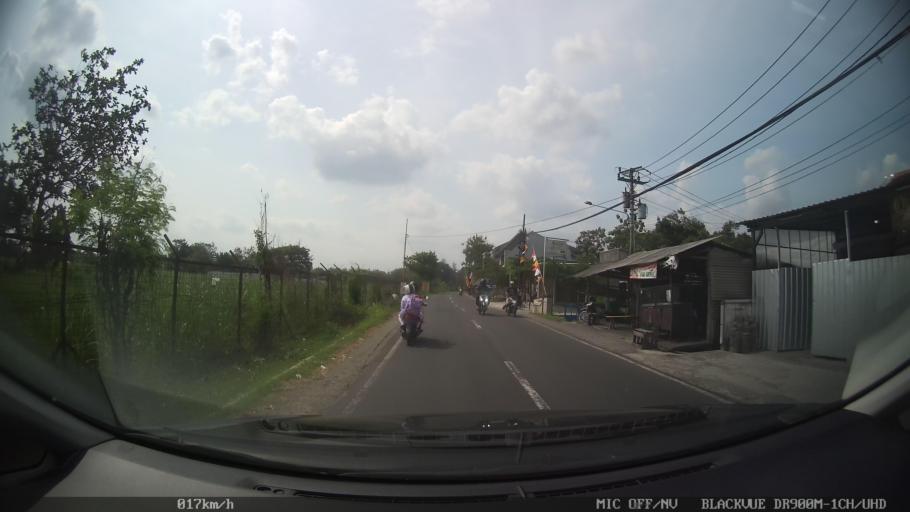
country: ID
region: Daerah Istimewa Yogyakarta
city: Depok
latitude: -7.8052
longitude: 110.4282
